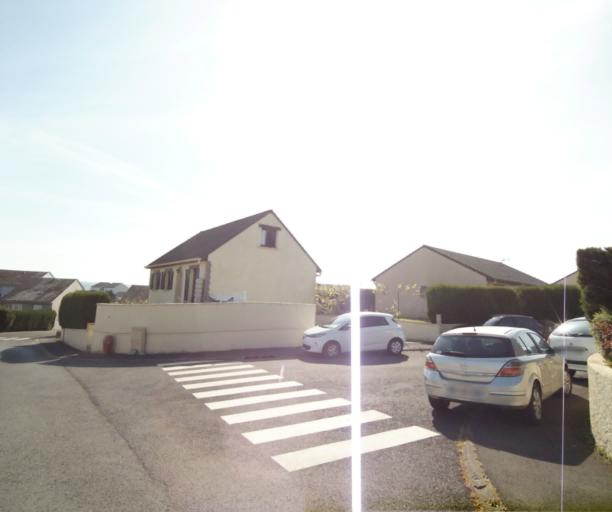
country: FR
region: Champagne-Ardenne
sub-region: Departement des Ardennes
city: La Francheville
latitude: 49.7390
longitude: 4.7156
